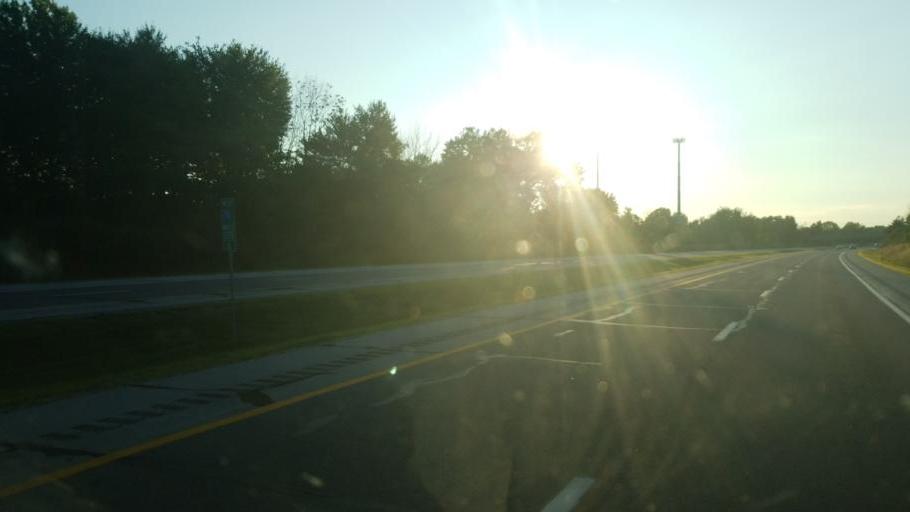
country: US
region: Ohio
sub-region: Mahoning County
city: Canfield
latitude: 41.0391
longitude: -80.7550
